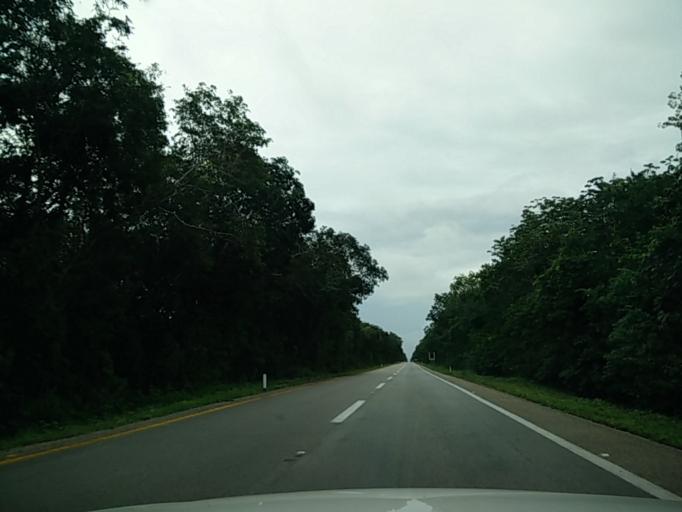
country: MX
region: Quintana Roo
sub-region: Lazaro Cardenas
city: Ignacio Zaragoza
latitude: 20.8939
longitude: -87.5079
